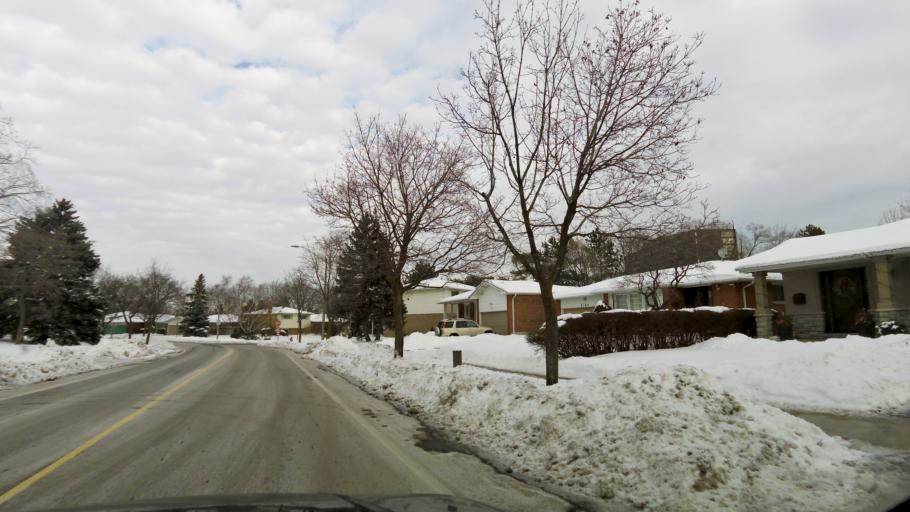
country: CA
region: Ontario
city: Mississauga
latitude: 43.5266
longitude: -79.6637
